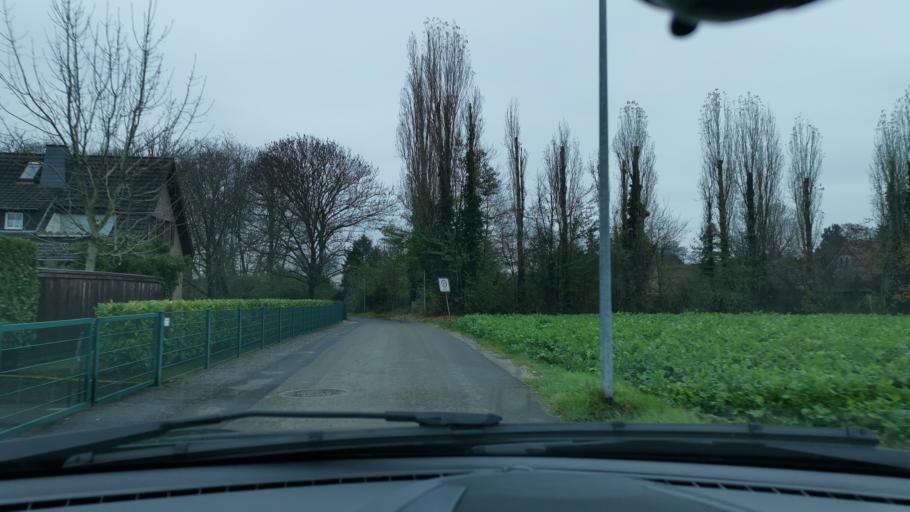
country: DE
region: North Rhine-Westphalia
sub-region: Regierungsbezirk Dusseldorf
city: Neubrueck
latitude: 51.1165
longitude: 6.6991
